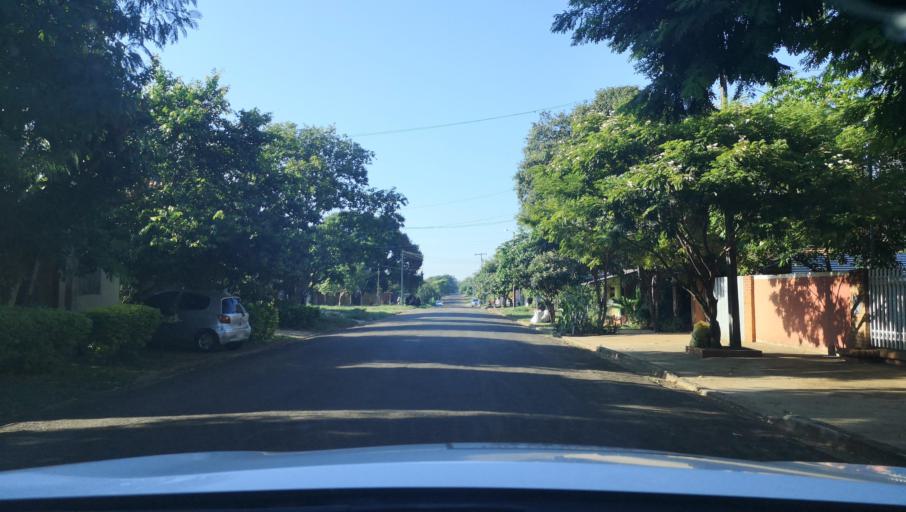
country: PY
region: Itapua
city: Carmen del Parana
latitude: -27.1621
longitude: -56.2446
